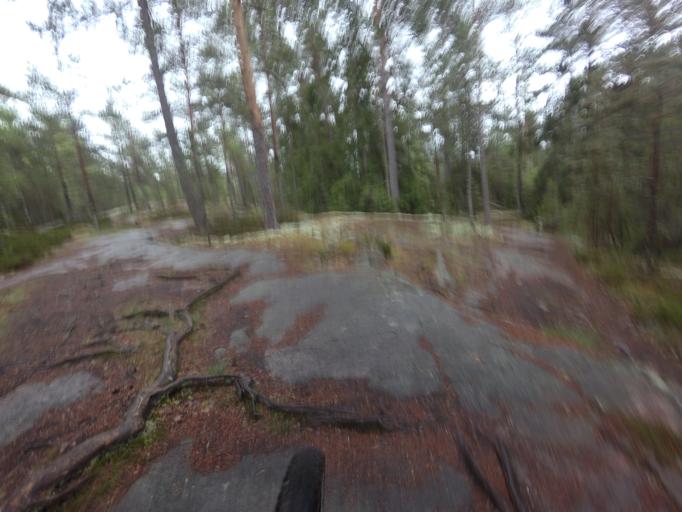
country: FI
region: Uusimaa
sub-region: Helsinki
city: Kauniainen
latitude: 60.1860
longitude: 24.7103
